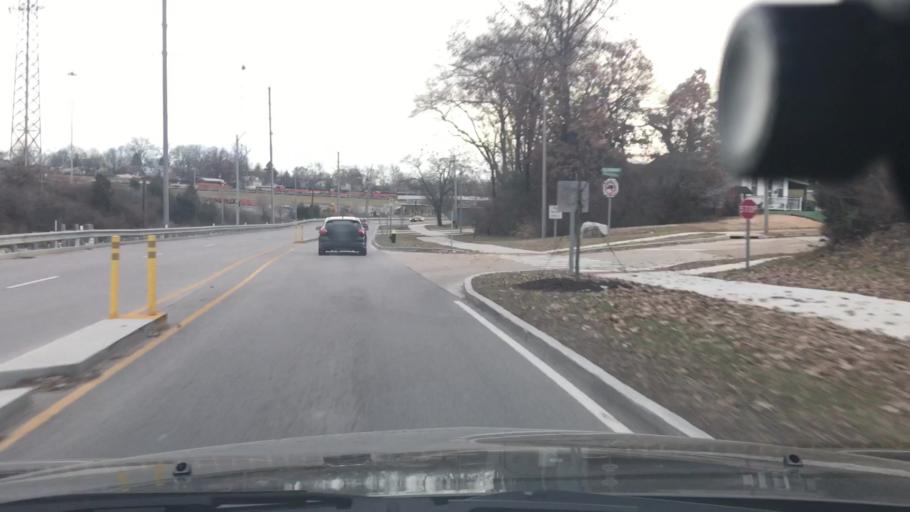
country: US
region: Missouri
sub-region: Saint Louis County
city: Maplewood
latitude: 38.6052
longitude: -90.3142
